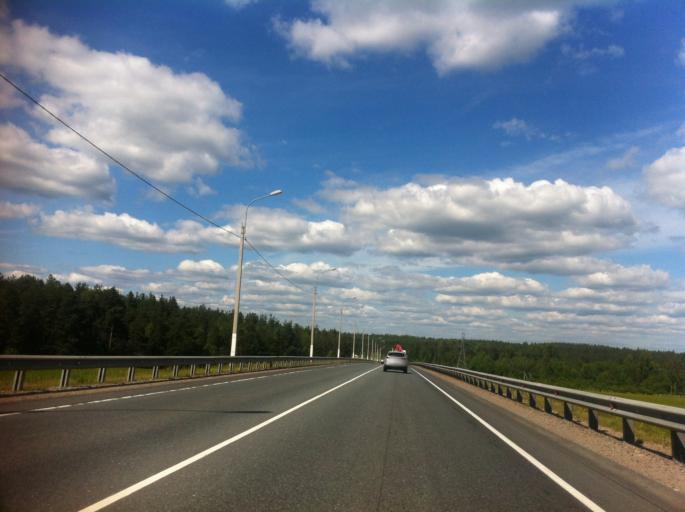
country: RU
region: Leningrad
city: Luga
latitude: 58.6980
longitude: 29.8794
